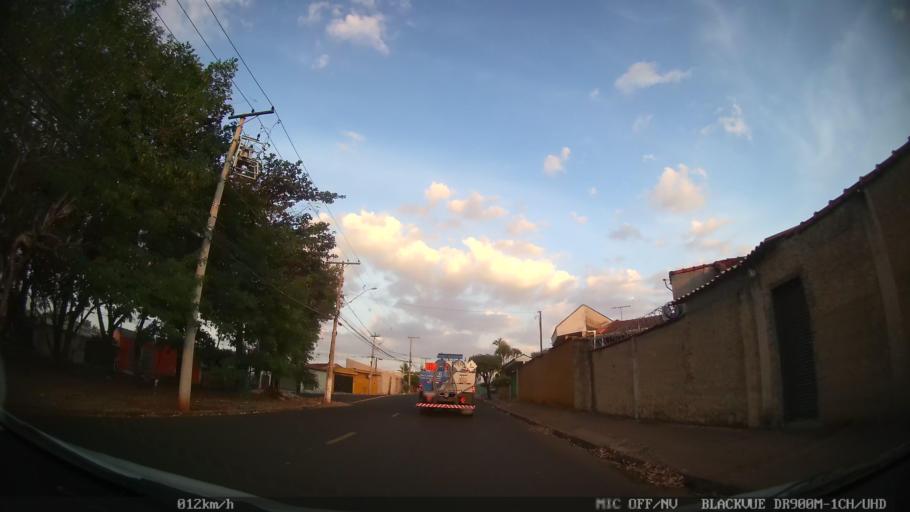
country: BR
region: Sao Paulo
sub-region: Ribeirao Preto
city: Ribeirao Preto
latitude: -21.1236
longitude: -47.8164
